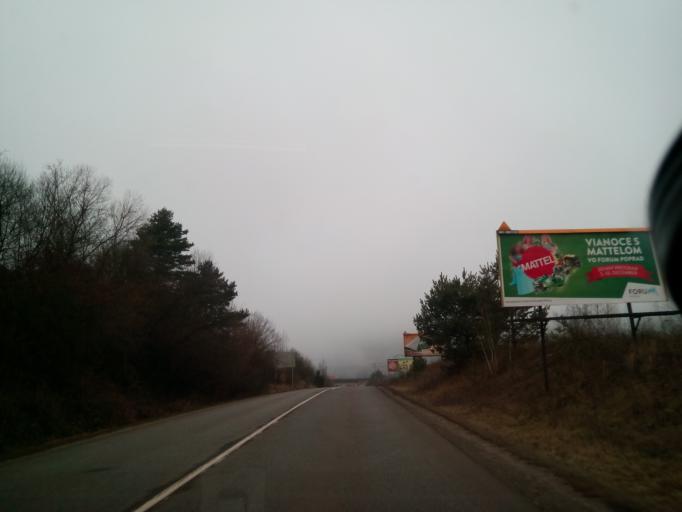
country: SK
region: Kosicky
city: Krompachy
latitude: 48.9221
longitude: 20.8608
